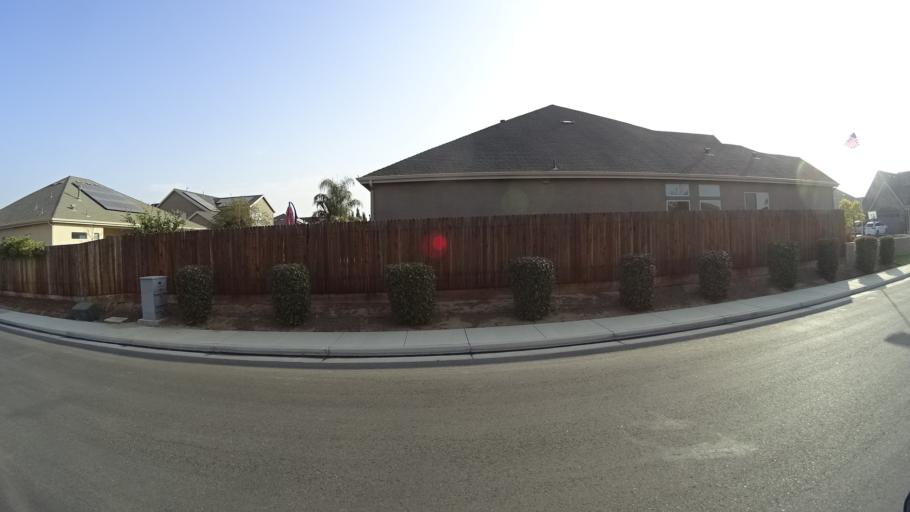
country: US
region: California
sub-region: Kern County
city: Greenacres
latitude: 35.4323
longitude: -119.1069
